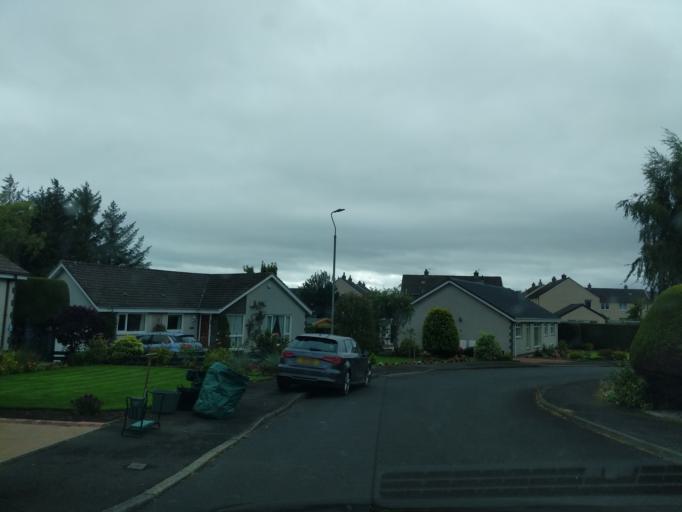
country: GB
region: Scotland
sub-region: The Scottish Borders
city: Saint Boswells
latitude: 55.5720
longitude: -2.6399
